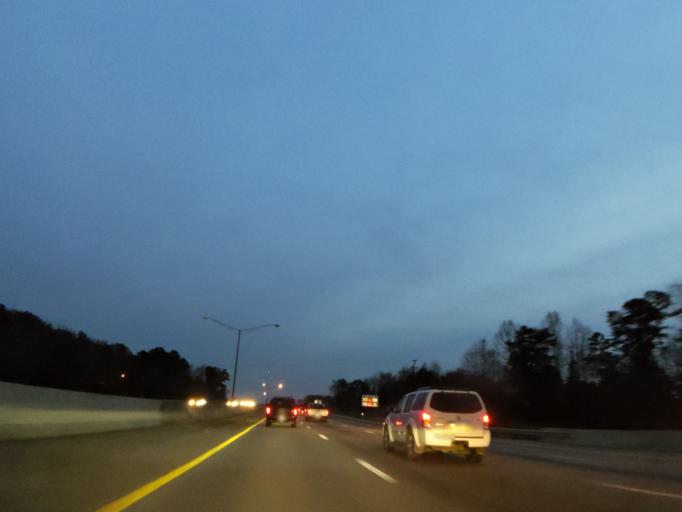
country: US
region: Kentucky
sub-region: Laurel County
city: London
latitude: 37.1241
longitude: -84.1068
